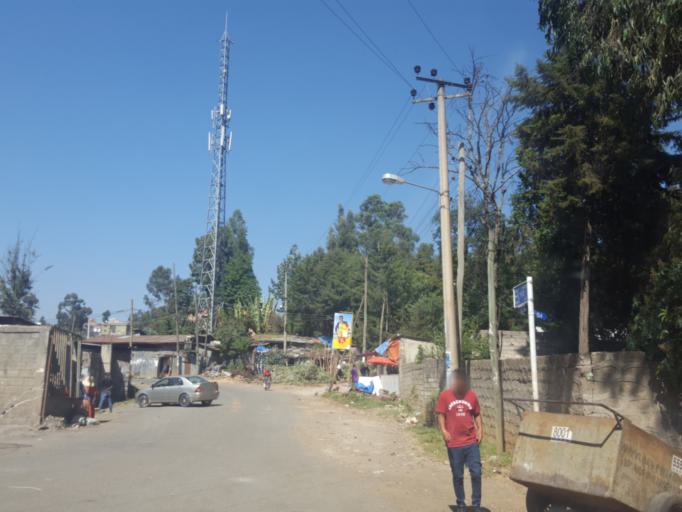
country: ET
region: Adis Abeba
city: Addis Ababa
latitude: 9.0549
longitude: 38.7394
